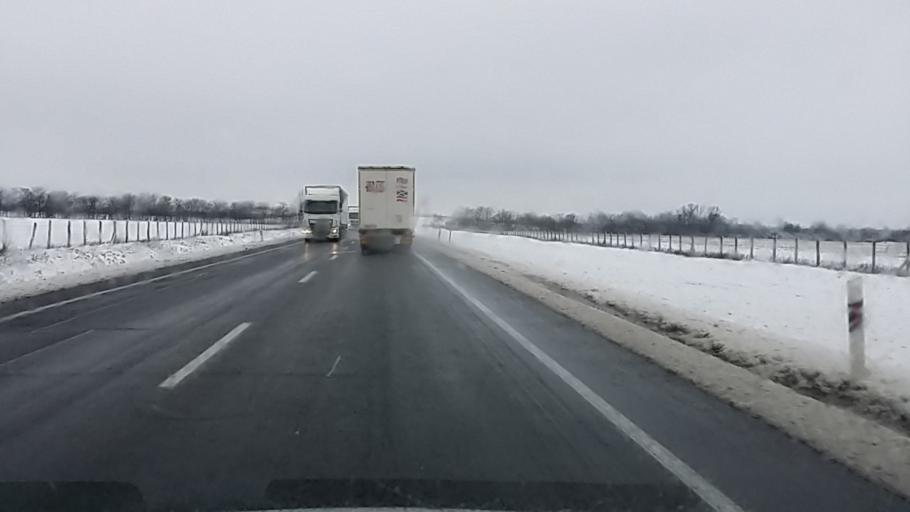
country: HU
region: Gyor-Moson-Sopron
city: Rajka
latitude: 47.9178
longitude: 17.1783
